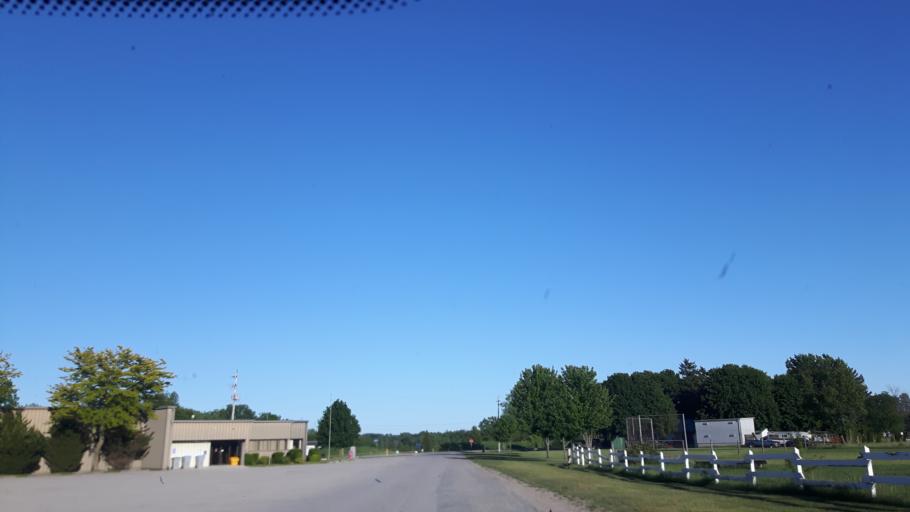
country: CA
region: Ontario
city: Goderich
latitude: 43.6443
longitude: -81.6040
